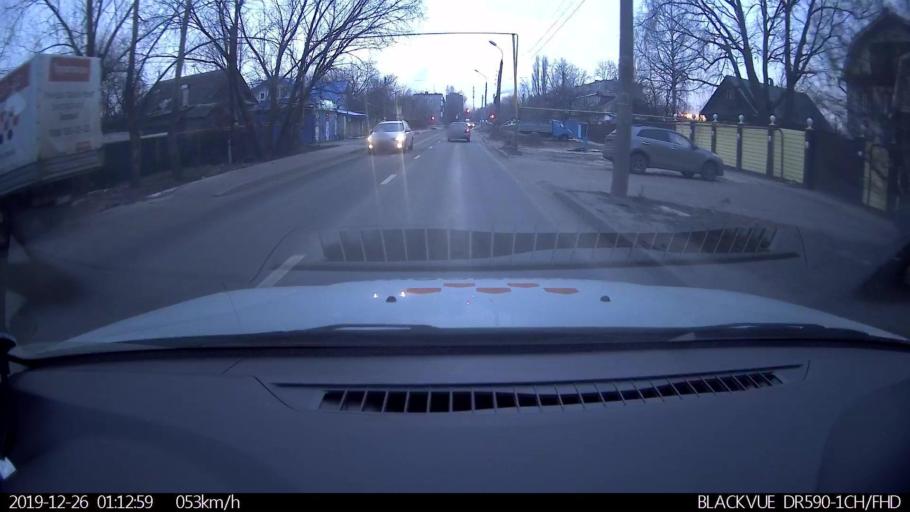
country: RU
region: Nizjnij Novgorod
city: Nizhniy Novgorod
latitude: 56.2803
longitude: 43.9127
